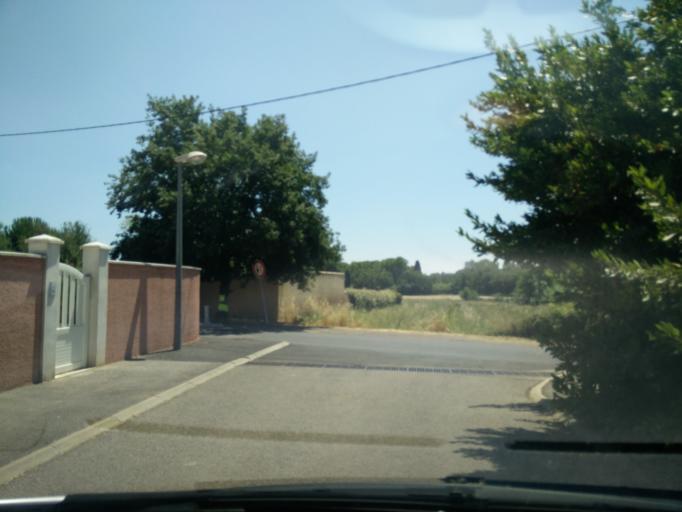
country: FR
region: Languedoc-Roussillon
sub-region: Departement de l'Herault
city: Saint-Christol
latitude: 43.7186
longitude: 4.0966
